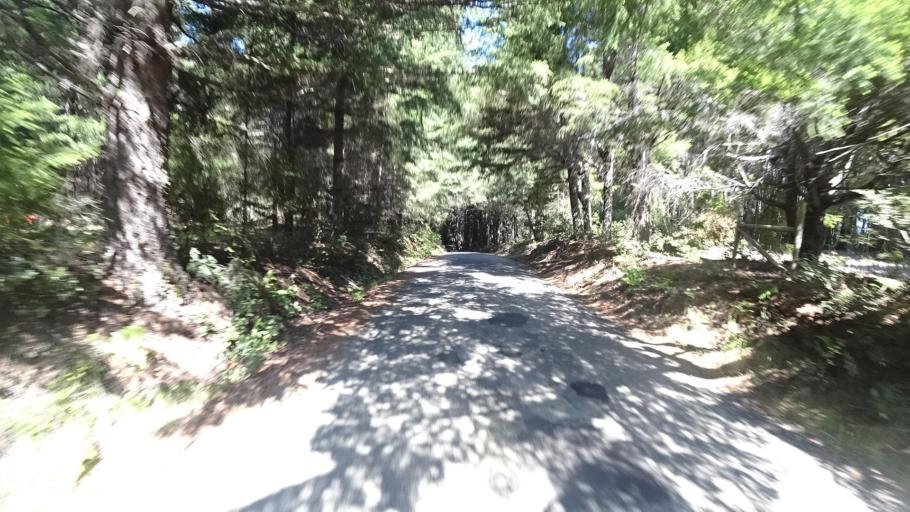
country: US
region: California
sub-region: Humboldt County
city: Redway
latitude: 40.1849
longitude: -124.0905
